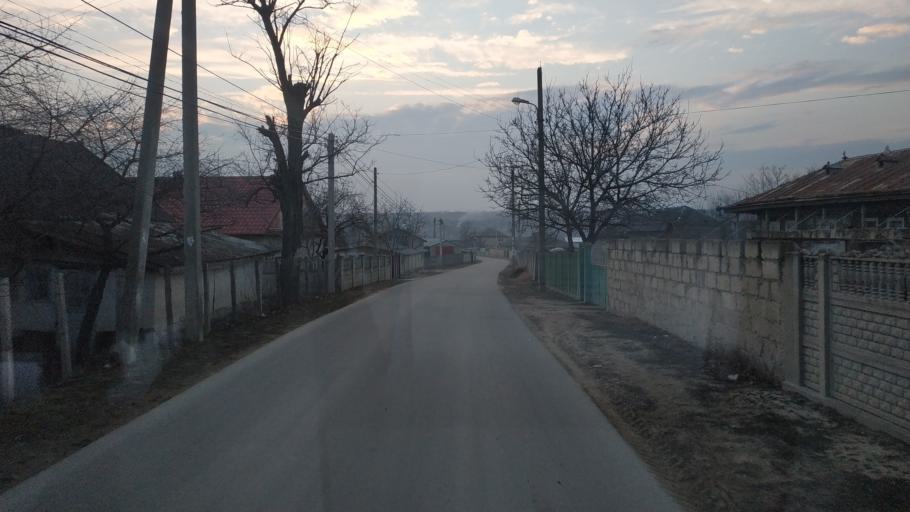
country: MD
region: Hincesti
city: Dancu
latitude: 46.6639
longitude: 28.3210
